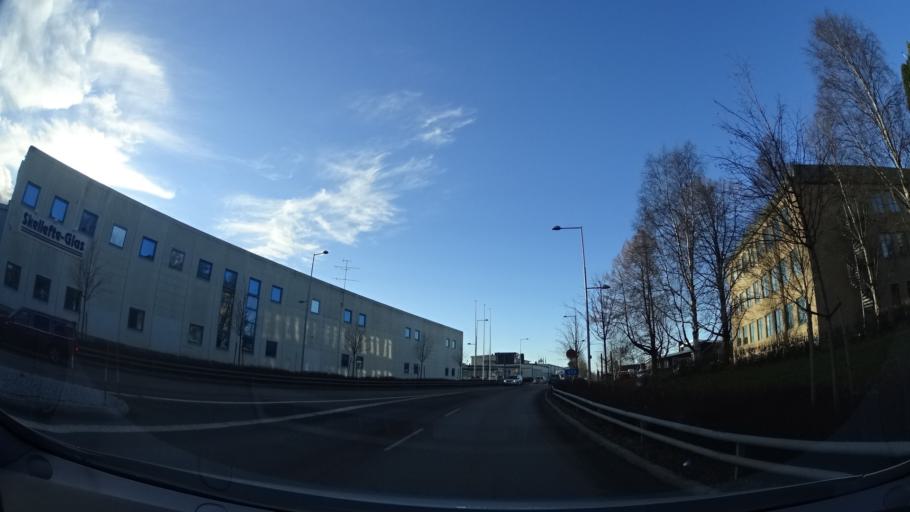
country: SE
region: Vaesterbotten
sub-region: Skelleftea Kommun
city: Skelleftea
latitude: 64.7528
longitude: 20.9729
